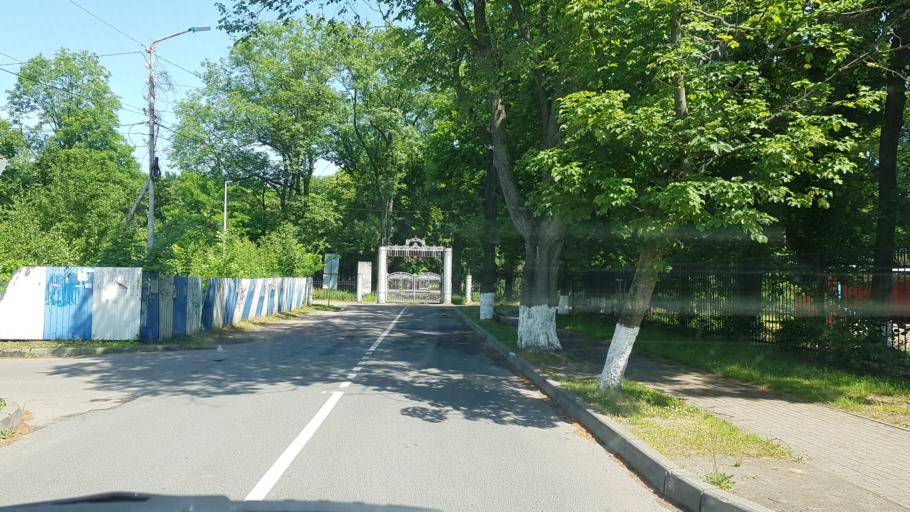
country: RU
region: Kaliningrad
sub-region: Gorod Kaliningrad
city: Baltiysk
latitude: 54.6474
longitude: 19.8930
